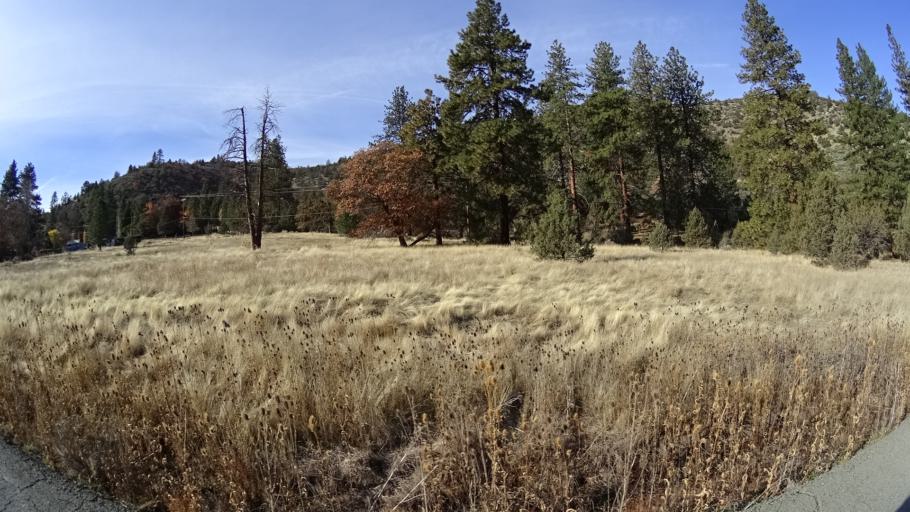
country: US
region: California
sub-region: Siskiyou County
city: Montague
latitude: 41.6014
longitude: -122.5776
